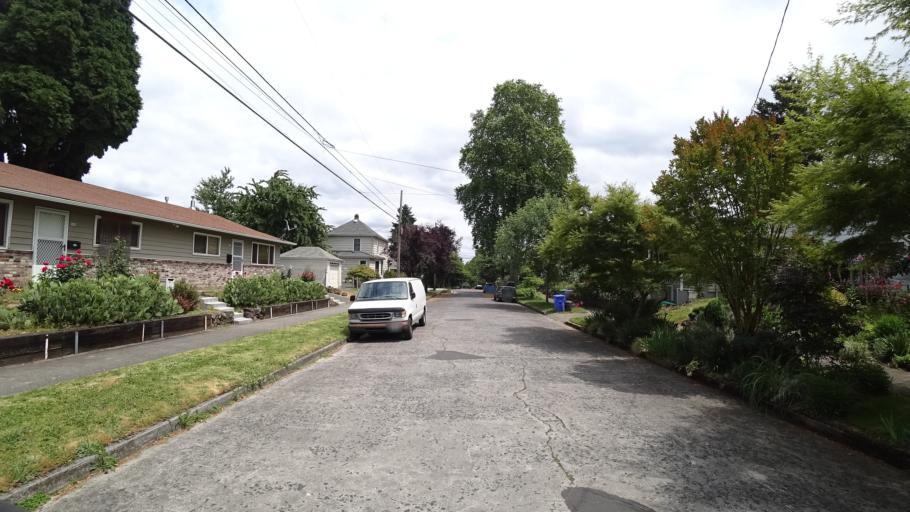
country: US
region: Oregon
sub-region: Multnomah County
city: Portland
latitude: 45.4964
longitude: -122.6568
